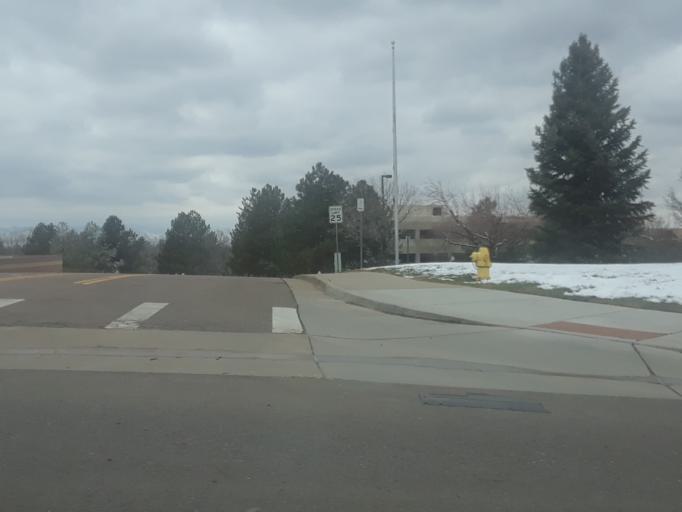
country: US
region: Colorado
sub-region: Arapahoe County
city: Centennial
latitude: 39.5761
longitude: -104.8816
